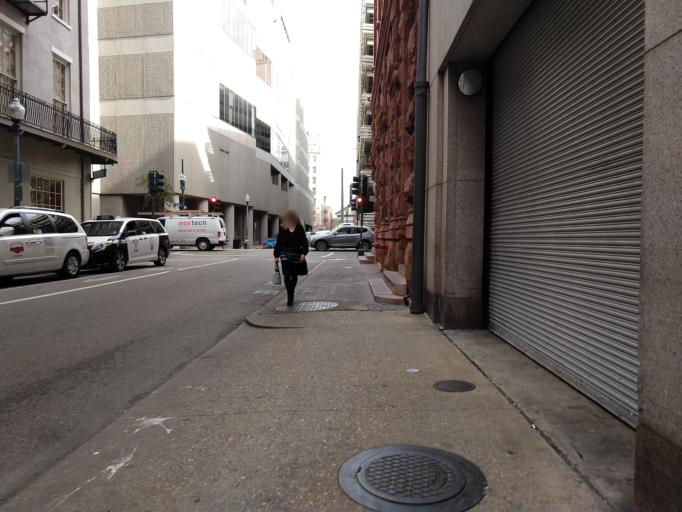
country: US
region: Louisiana
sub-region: Orleans Parish
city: New Orleans
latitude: 29.9518
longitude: -90.0689
